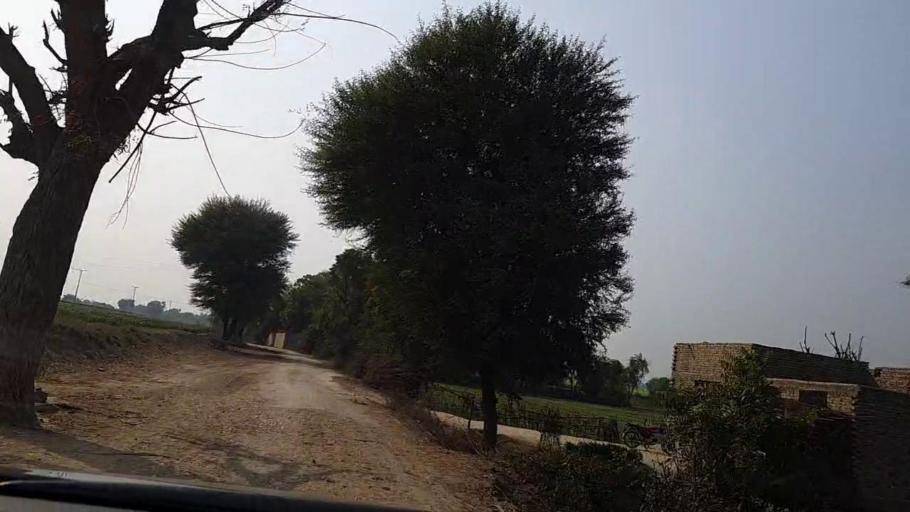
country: PK
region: Sindh
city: Sakrand
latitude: 26.1512
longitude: 68.2453
